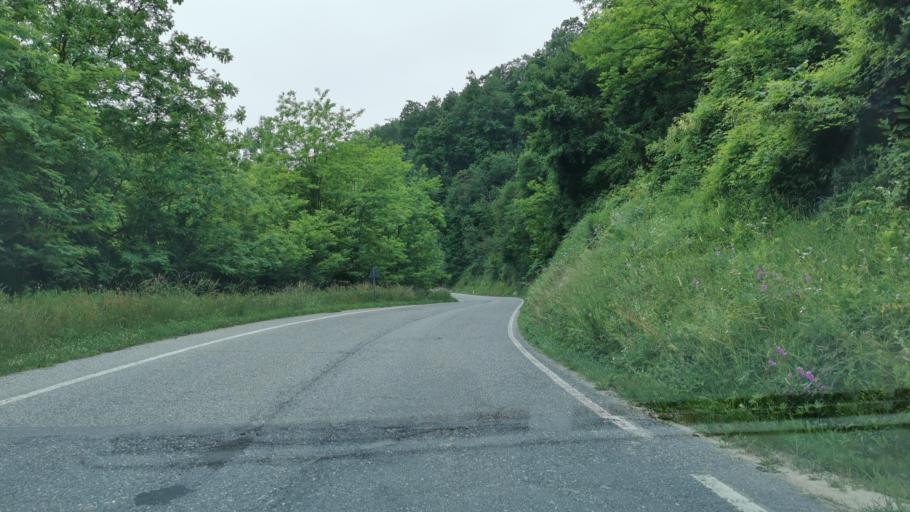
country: IT
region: Piedmont
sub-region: Provincia di Cuneo
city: Ceva
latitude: 44.4049
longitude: 8.0480
